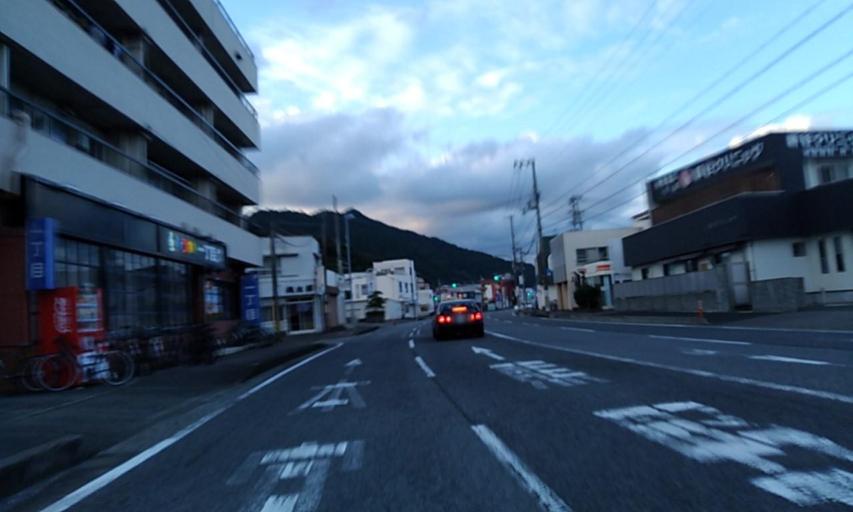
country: JP
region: Wakayama
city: Shingu
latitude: 33.7163
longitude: 135.9878
